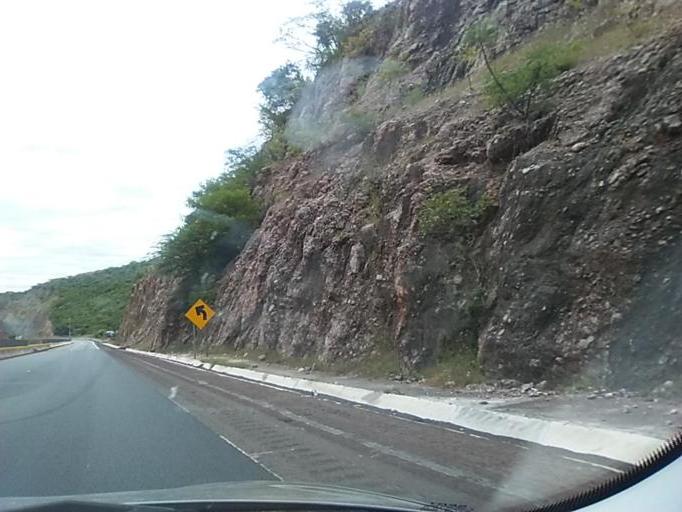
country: MX
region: Guerrero
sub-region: Huitzuco de los Figueroa
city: Ciudad de Huitzuco
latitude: 18.1983
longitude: -99.2067
